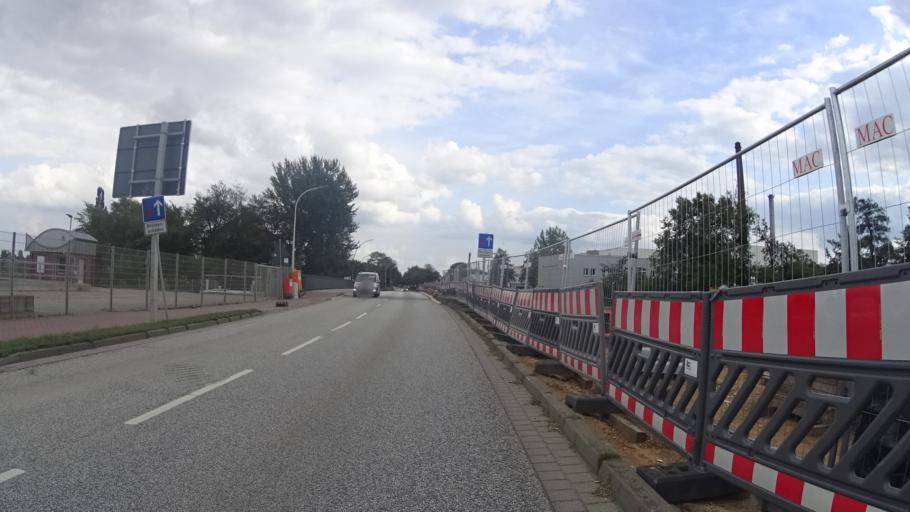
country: DE
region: Schleswig-Holstein
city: Gluckstadt
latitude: 53.7849
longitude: 9.4267
